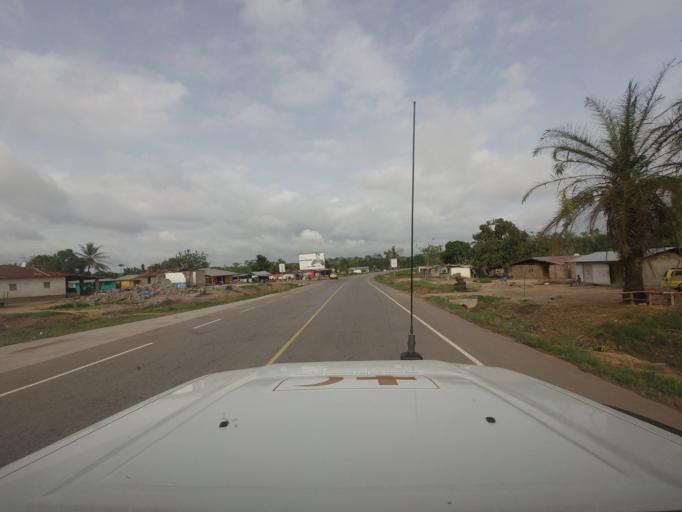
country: LR
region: Bong
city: Gbarnga
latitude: 7.0017
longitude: -9.2895
